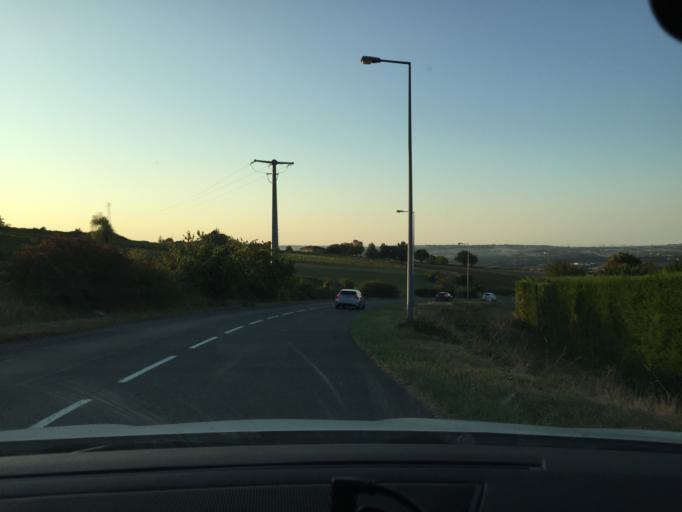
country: FR
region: Rhone-Alpes
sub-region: Departement du Rhone
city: Lozanne
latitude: 45.8699
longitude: 4.6715
